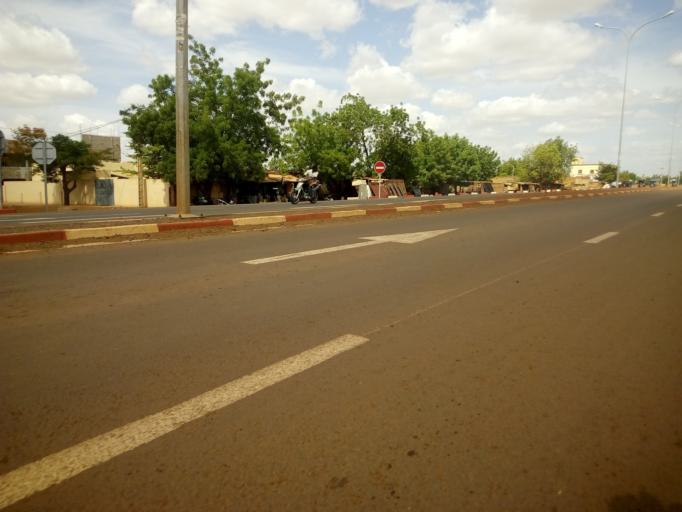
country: ML
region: Segou
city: Segou
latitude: 13.4289
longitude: -6.2225
